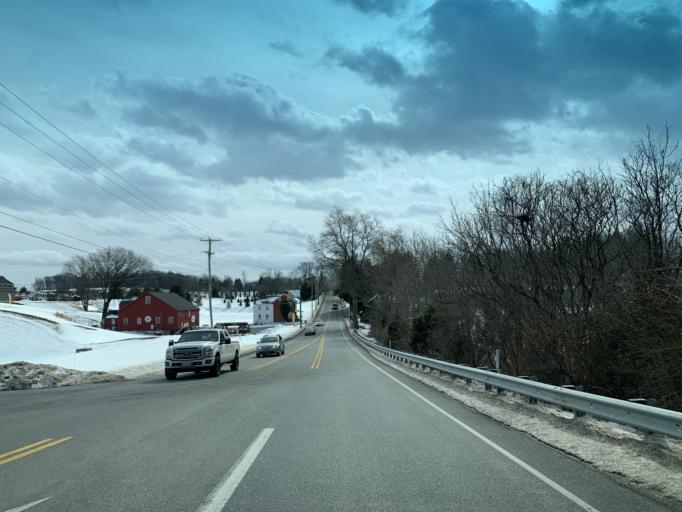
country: US
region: Pennsylvania
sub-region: York County
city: Shrewsbury
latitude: 39.8050
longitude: -76.6809
